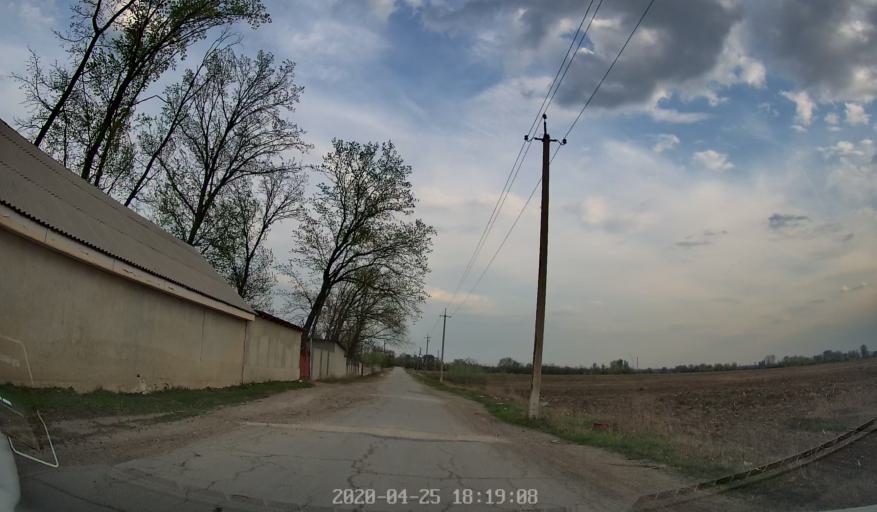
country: MD
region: Criuleni
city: Criuleni
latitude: 47.1608
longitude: 29.1296
